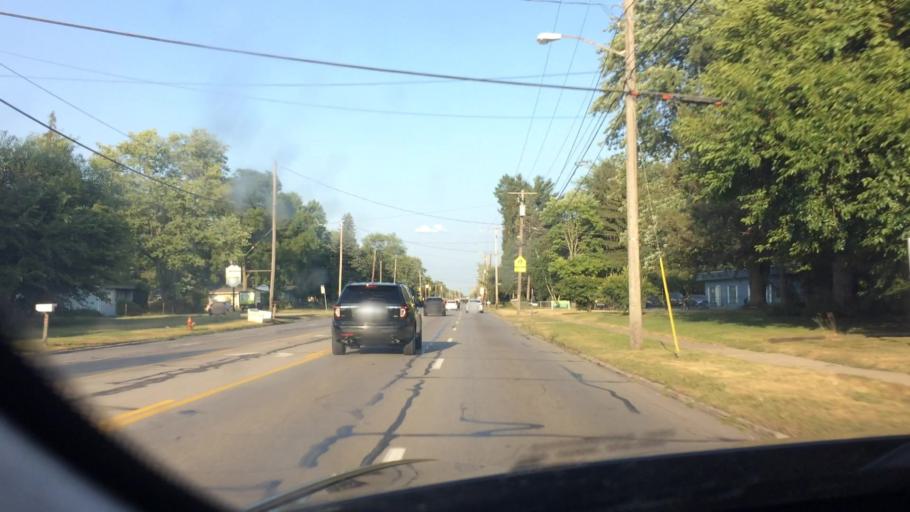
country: US
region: Ohio
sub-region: Lucas County
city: Ottawa Hills
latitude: 41.6536
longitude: -83.6783
